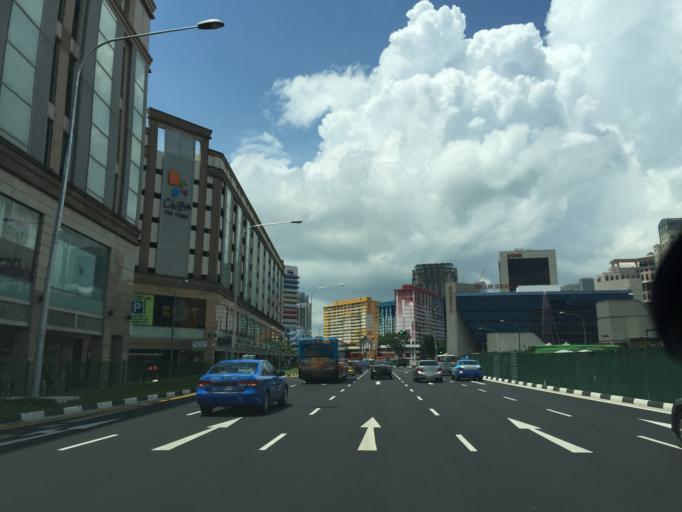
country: SG
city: Singapore
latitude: 1.3049
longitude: 103.8513
